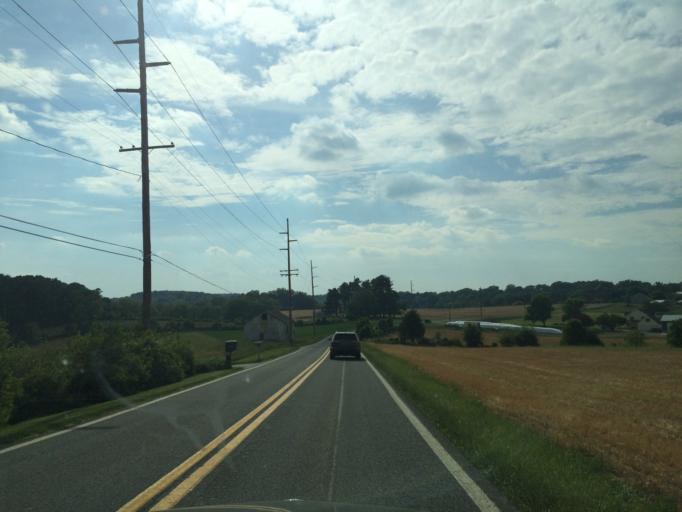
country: US
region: Maryland
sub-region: Baltimore County
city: Reisterstown
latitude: 39.4693
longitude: -76.9041
